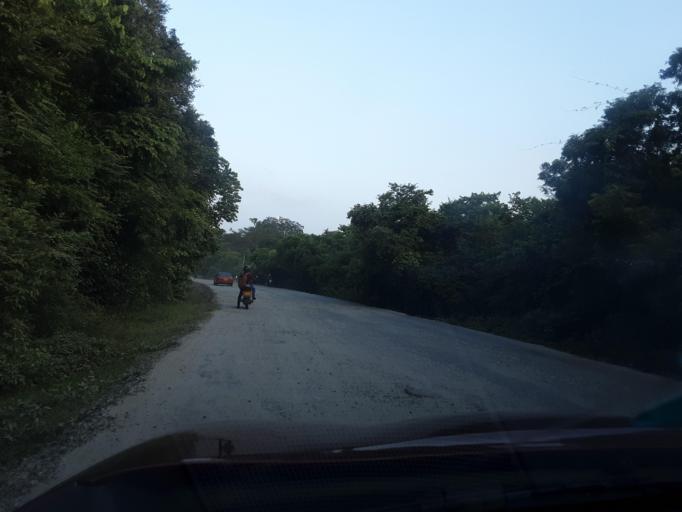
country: LK
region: Central
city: Dambulla
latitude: 7.8102
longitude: 80.7698
